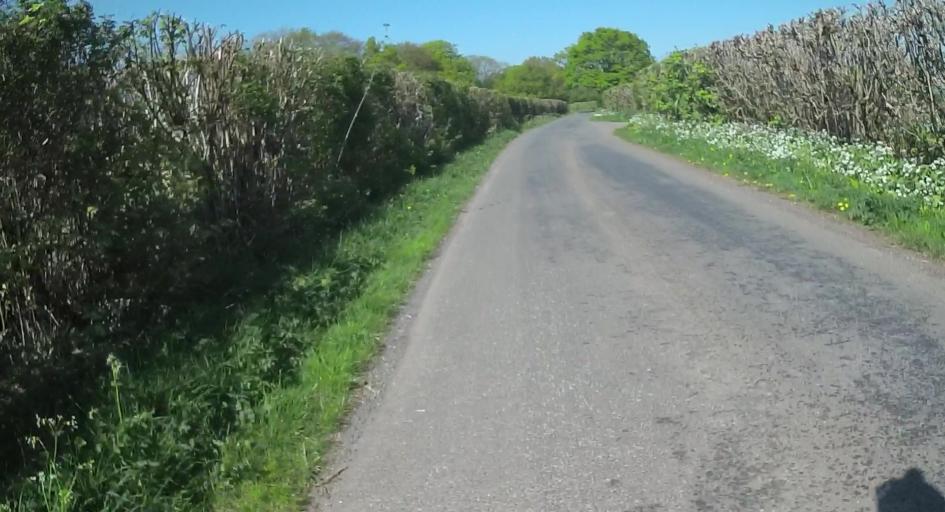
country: GB
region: England
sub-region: Hampshire
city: Four Marks
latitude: 51.1355
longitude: -1.0409
